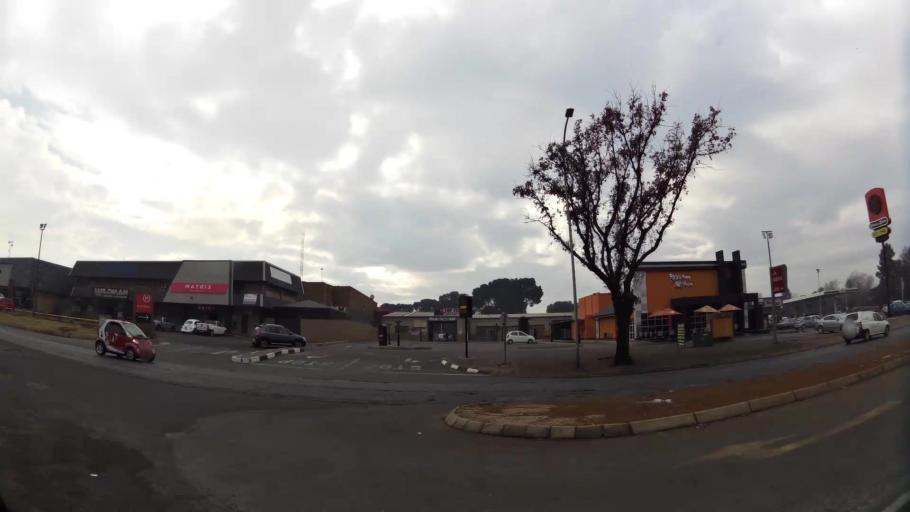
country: ZA
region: Gauteng
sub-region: Sedibeng District Municipality
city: Vanderbijlpark
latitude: -26.7028
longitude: 27.8347
